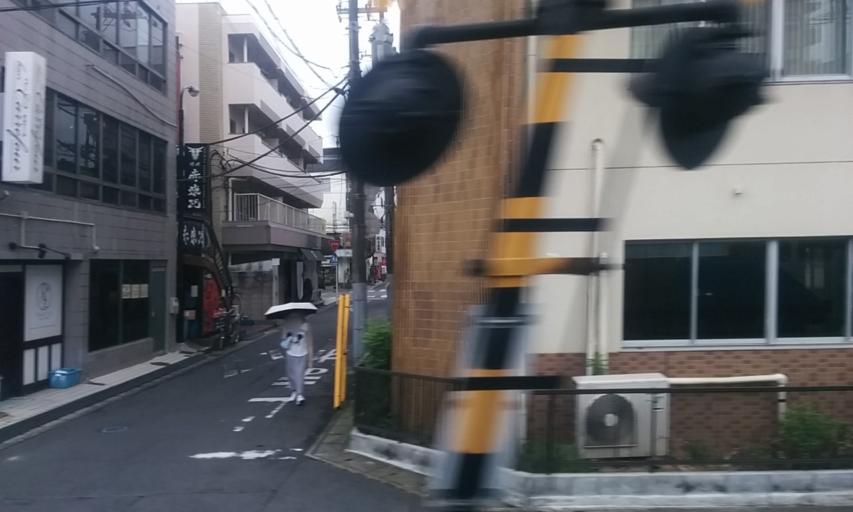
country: JP
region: Chiba
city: Nagareyama
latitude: 35.8276
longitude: 139.9201
